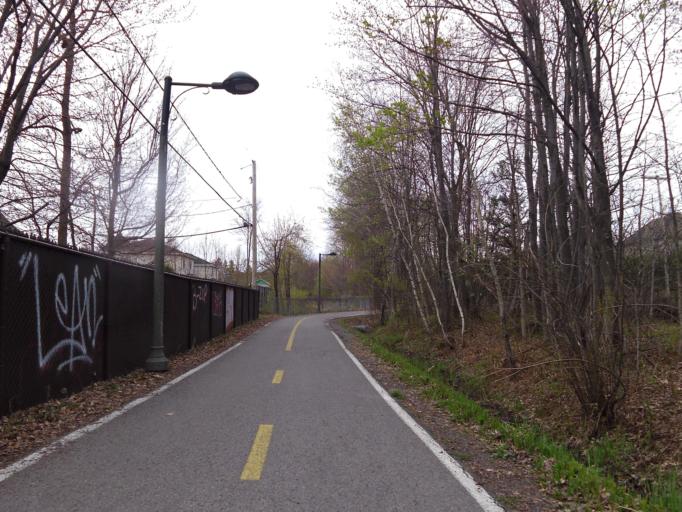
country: CA
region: Quebec
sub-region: Laurentides
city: Sainte-Marthe-sur-le-Lac
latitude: 45.5342
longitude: -73.9261
